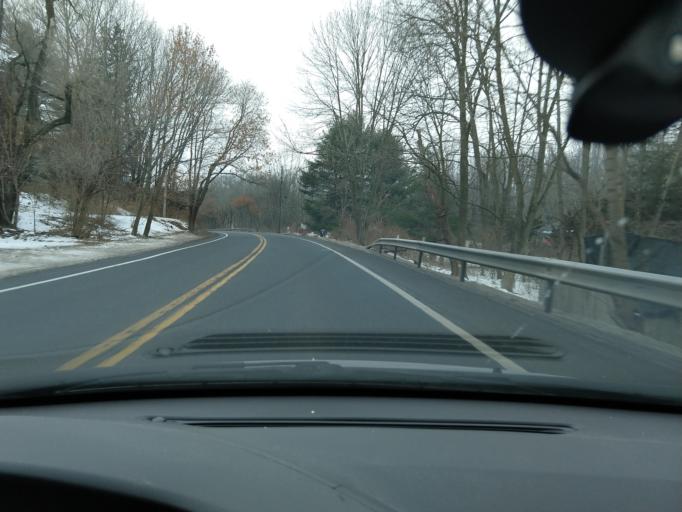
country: US
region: Pennsylvania
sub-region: Lehigh County
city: Macungie
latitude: 40.4624
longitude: -75.5503
